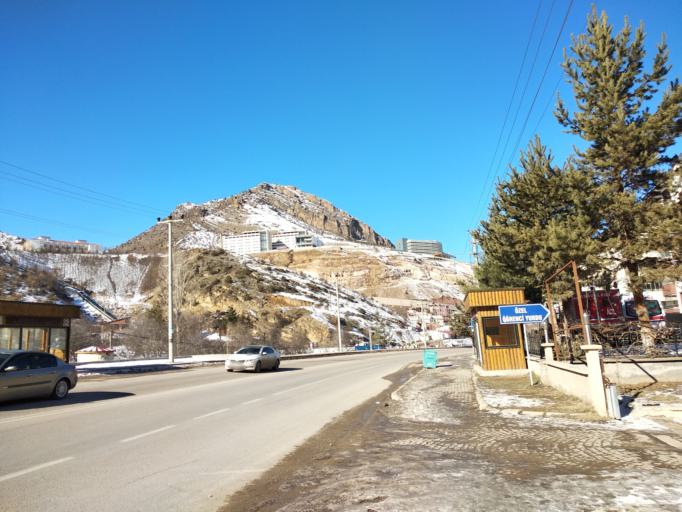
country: TR
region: Gumushane
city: Gumushkhane
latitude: 40.4377
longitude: 39.5056
